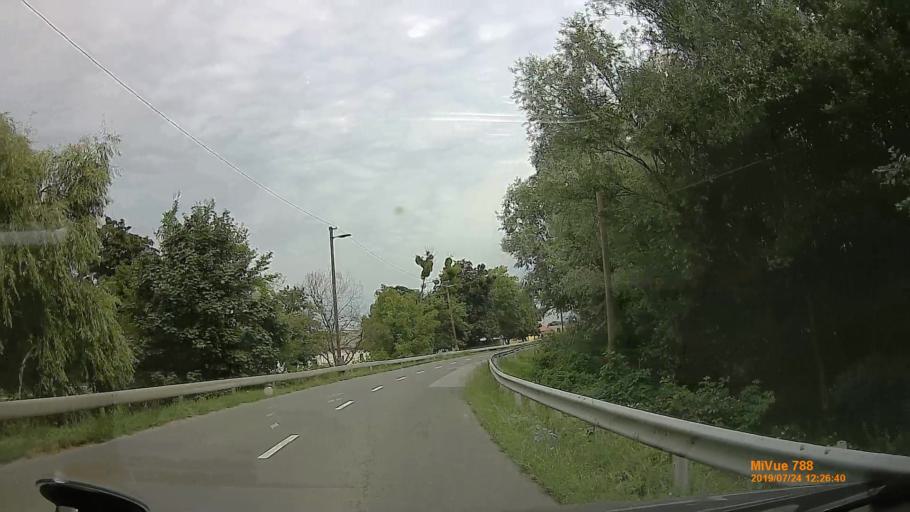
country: HU
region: Szabolcs-Szatmar-Bereg
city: Vasarosnameny
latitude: 48.1309
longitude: 22.3421
